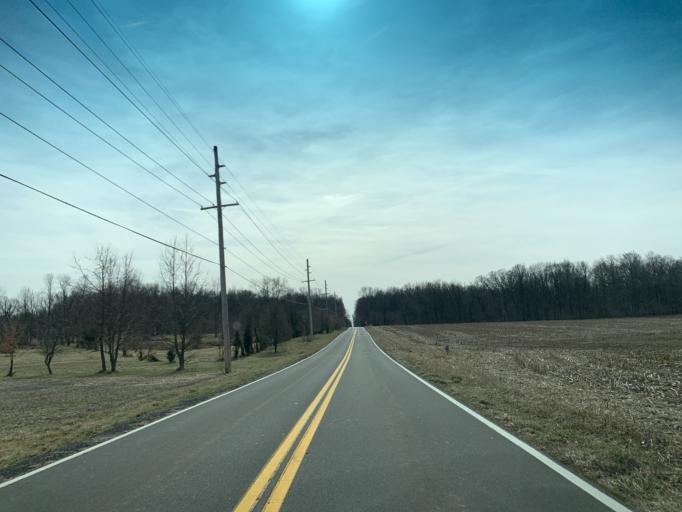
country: US
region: Maryland
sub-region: Frederick County
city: Buckeystown
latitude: 39.3340
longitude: -77.4539
